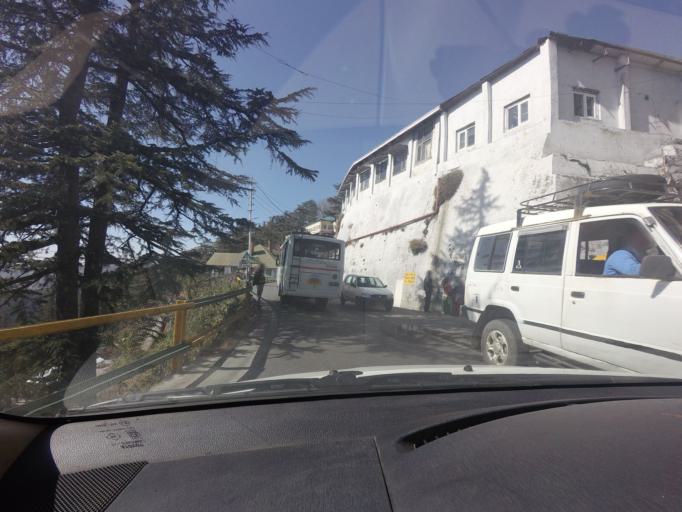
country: IN
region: Himachal Pradesh
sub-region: Shimla
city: Shimla
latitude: 31.1031
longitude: 77.1591
